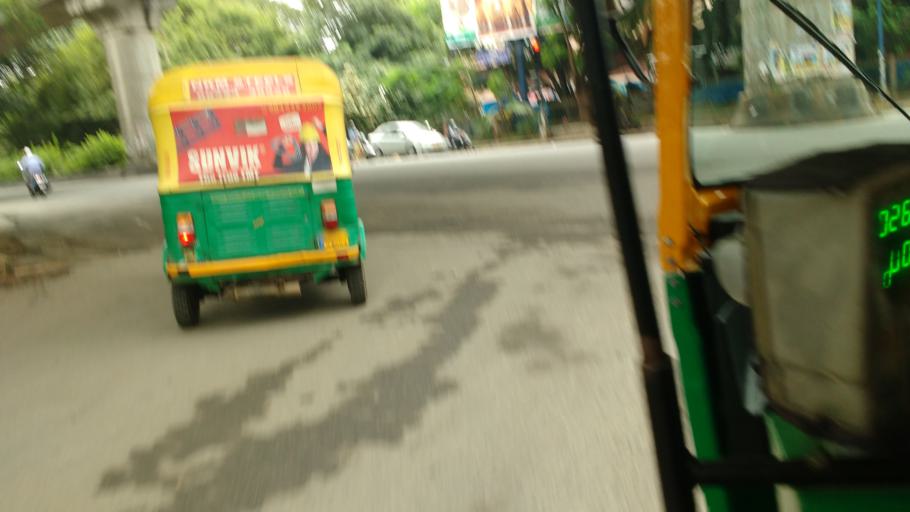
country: IN
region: Karnataka
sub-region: Bangalore Urban
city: Bangalore
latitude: 12.9731
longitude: 77.5384
